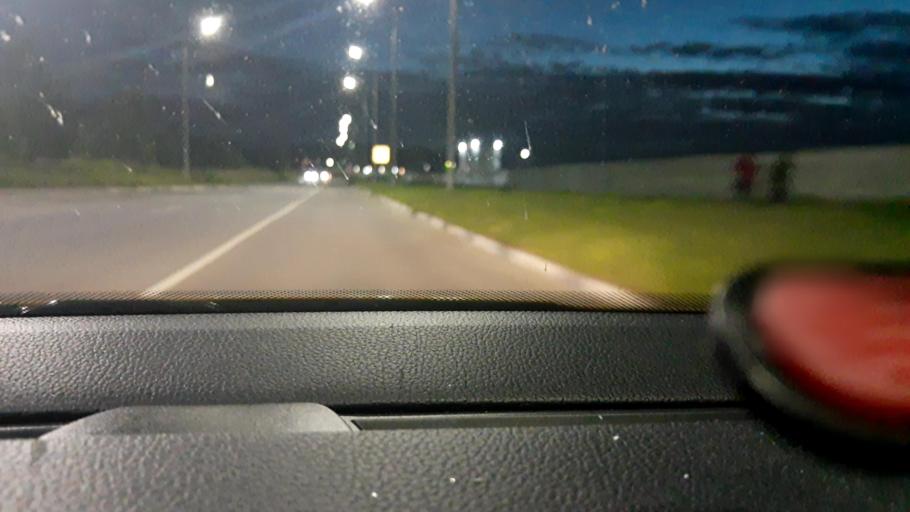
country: RU
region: Moskovskaya
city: Pirogovskiy
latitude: 55.9573
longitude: 37.6790
